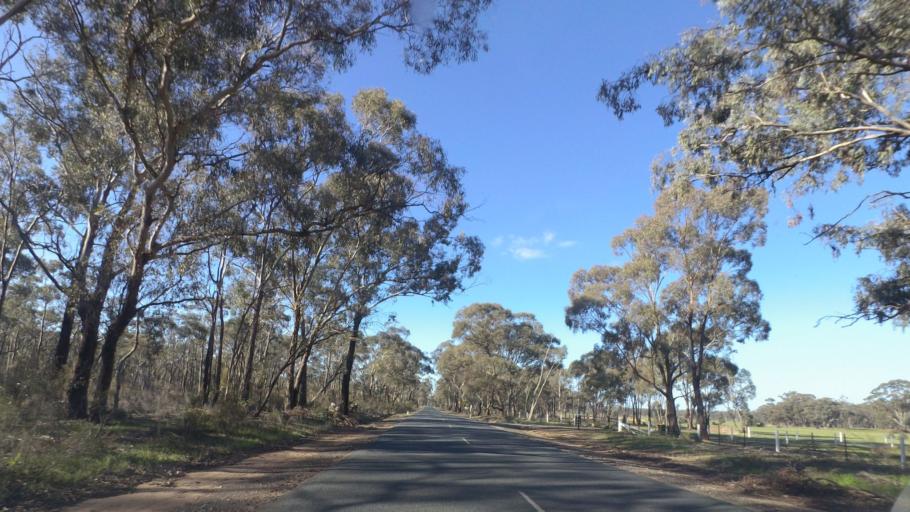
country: AU
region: Victoria
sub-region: Greater Bendigo
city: Epsom
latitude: -36.6632
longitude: 144.4496
